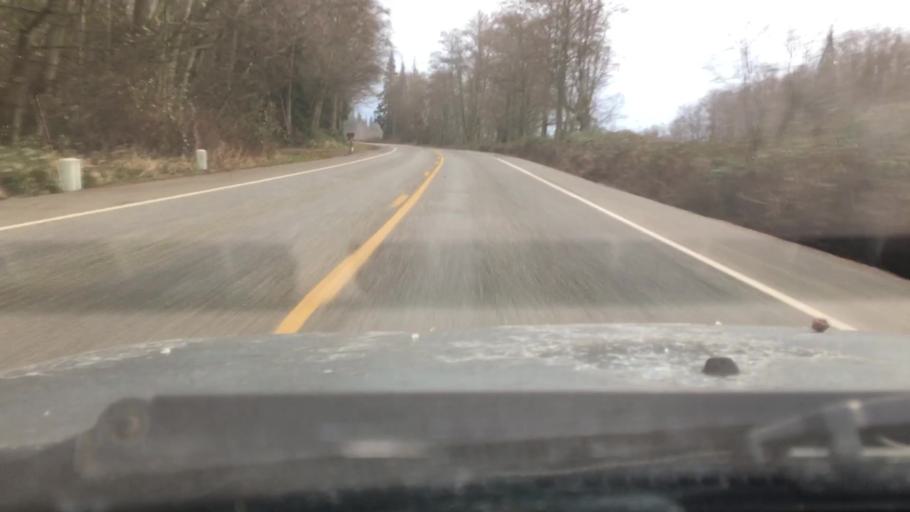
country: US
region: Washington
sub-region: Whatcom County
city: Birch Bay
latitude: 48.8581
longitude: -122.7014
